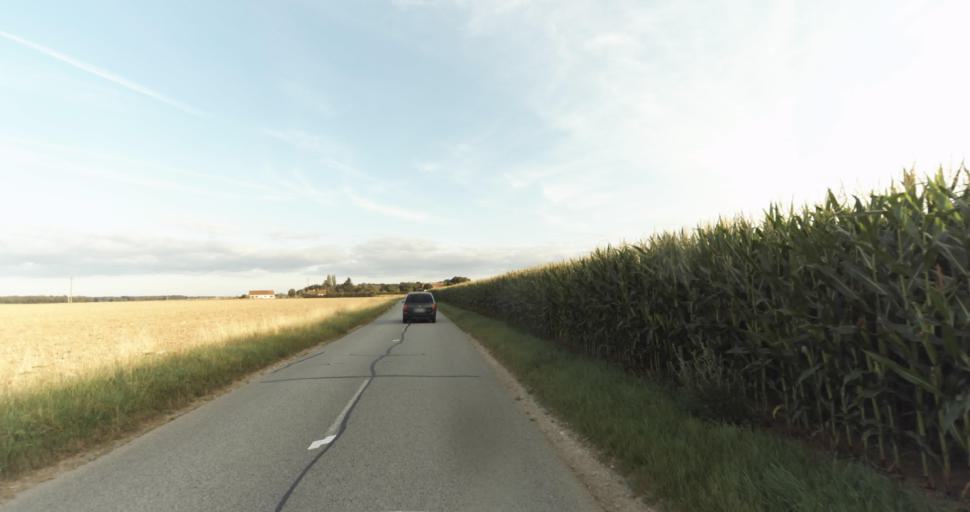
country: FR
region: Haute-Normandie
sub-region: Departement de l'Eure
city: Saint-Germain-sur-Avre
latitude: 48.8469
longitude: 1.2517
